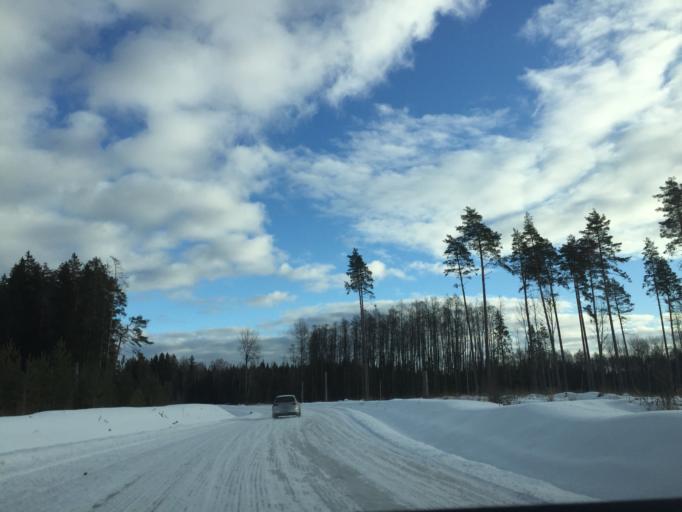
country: LV
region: Ogre
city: Jumprava
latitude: 56.5503
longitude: 24.8888
